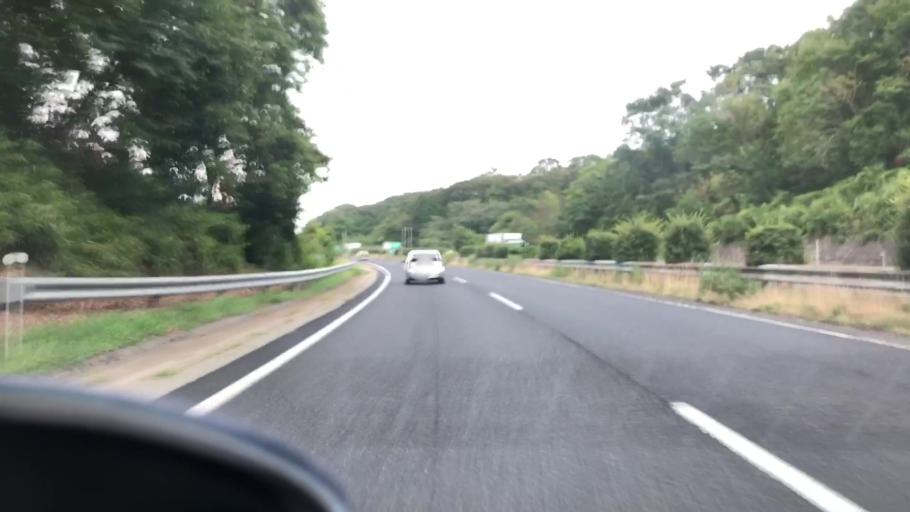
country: JP
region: Hyogo
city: Yashiro
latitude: 34.9100
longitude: 135.0459
